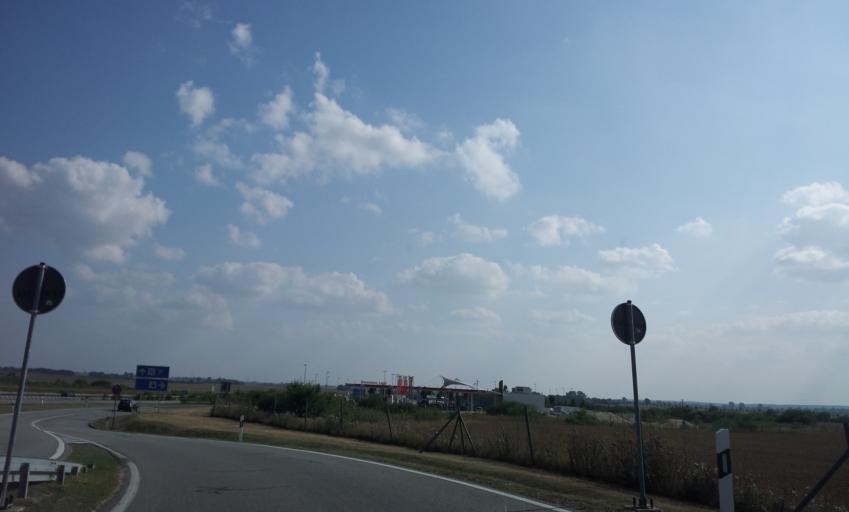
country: DE
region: Mecklenburg-Vorpommern
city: Jarmen
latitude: 53.8584
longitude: 13.3356
